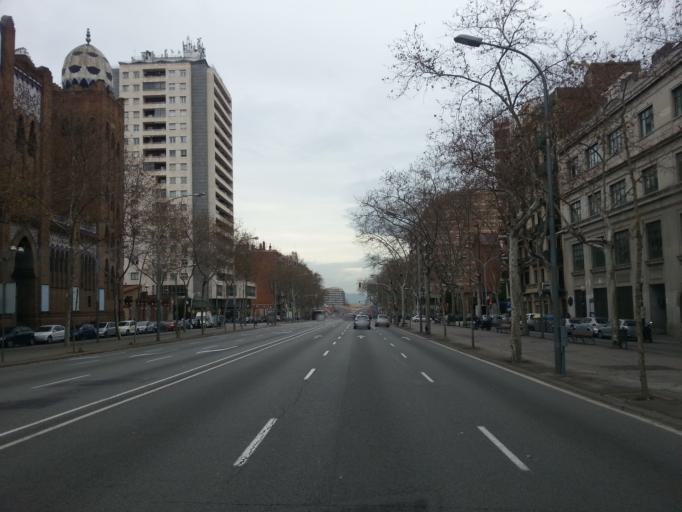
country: ES
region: Catalonia
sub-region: Provincia de Barcelona
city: Ciutat Vella
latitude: 41.3994
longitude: 2.1815
